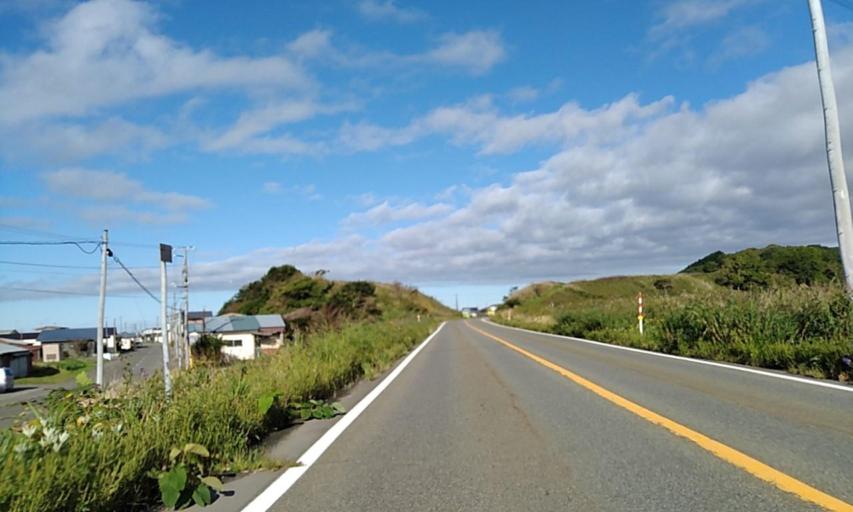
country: JP
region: Hokkaido
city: Shizunai-furukawacho
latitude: 42.2264
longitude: 142.6210
